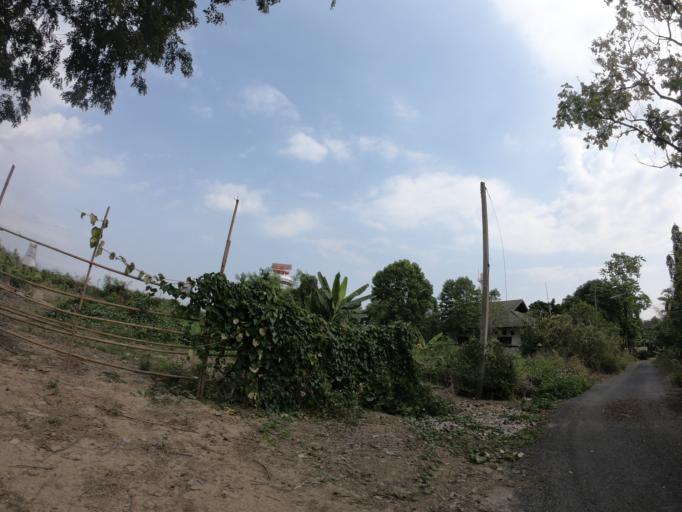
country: TH
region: Chiang Mai
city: Chiang Mai
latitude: 18.7588
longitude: 98.9665
